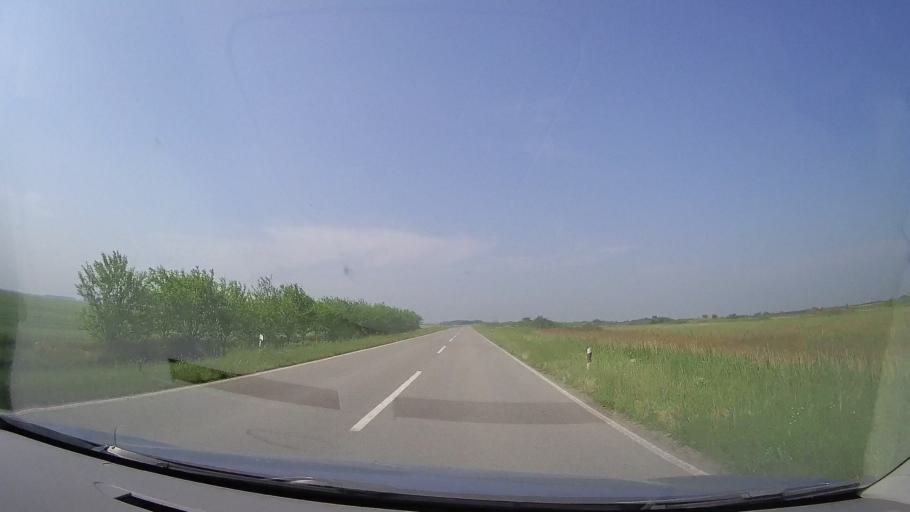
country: RS
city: Boka
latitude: 45.4022
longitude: 20.8161
